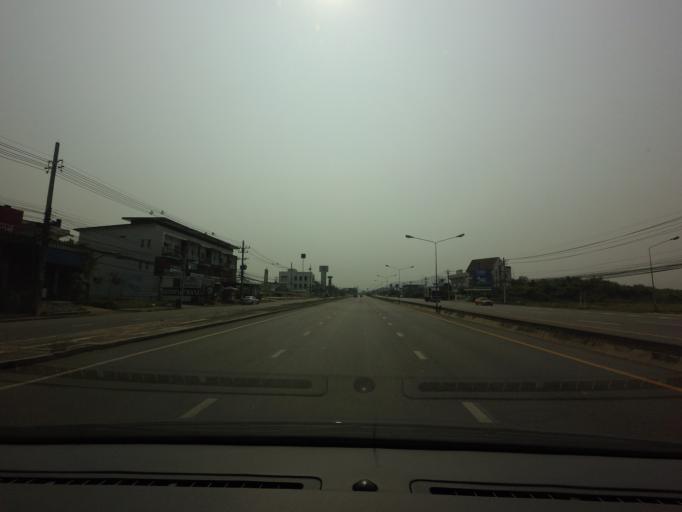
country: TH
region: Prachuap Khiri Khan
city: Pran Buri
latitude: 12.3805
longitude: 99.8930
